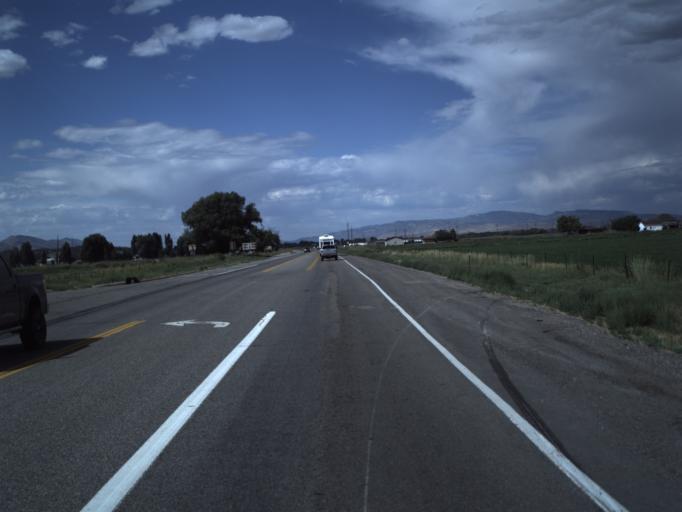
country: US
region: Utah
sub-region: Sevier County
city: Salina
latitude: 38.9648
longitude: -111.8600
